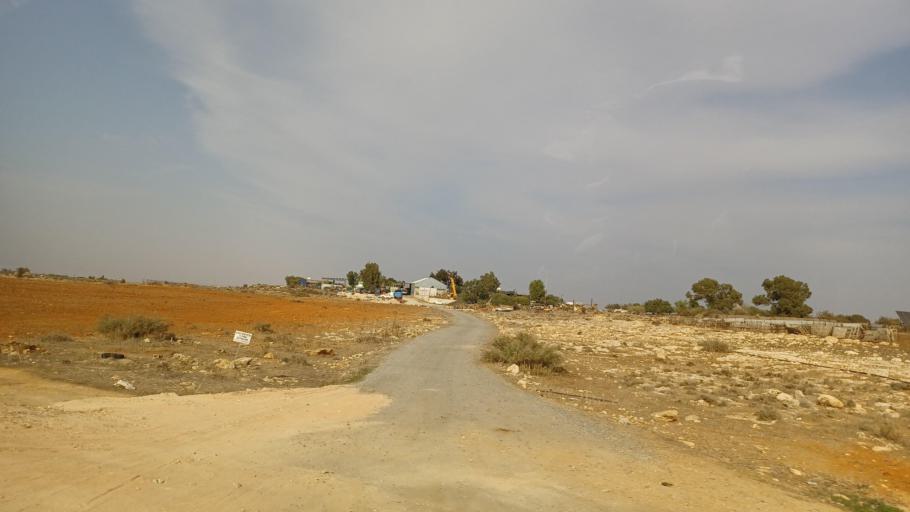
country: CY
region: Ammochostos
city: Frenaros
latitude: 35.0515
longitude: 33.9050
